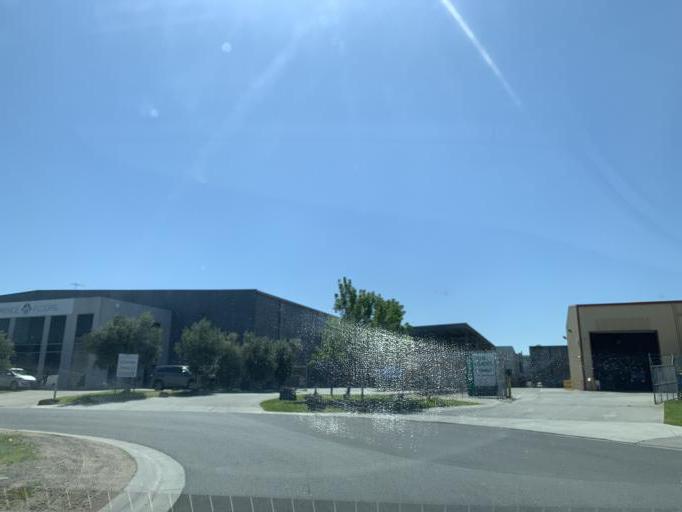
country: AU
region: Victoria
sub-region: Greater Dandenong
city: Dandenong
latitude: -38.0111
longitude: 145.2102
